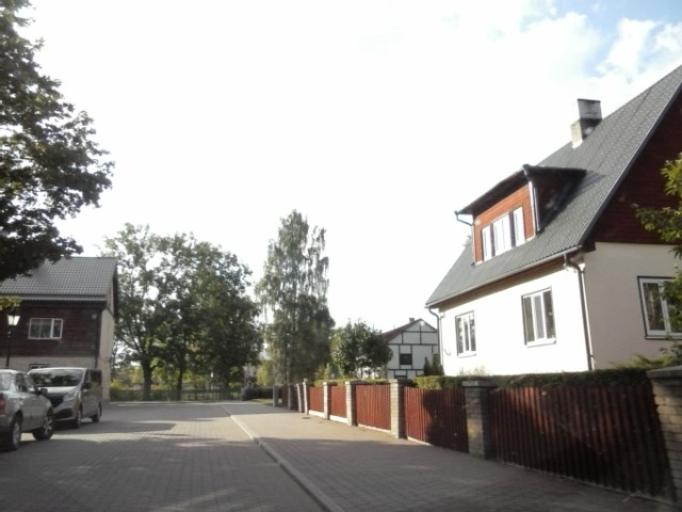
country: EE
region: Vorumaa
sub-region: Voru linn
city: Voru
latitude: 57.8447
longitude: 26.9927
